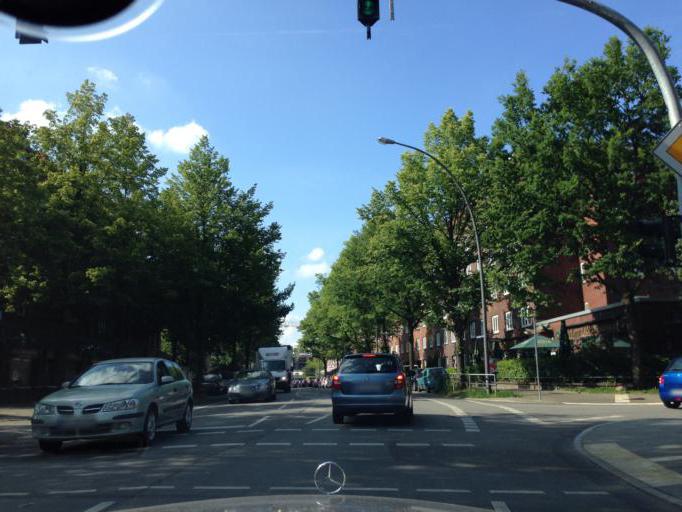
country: DE
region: Hamburg
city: Barmbek-Nord
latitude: 53.5962
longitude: 10.0434
